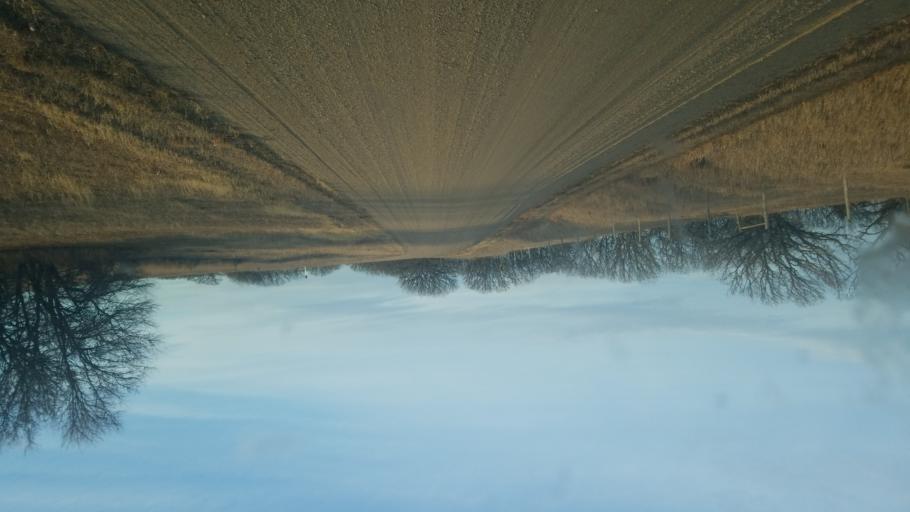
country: US
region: Nebraska
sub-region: Knox County
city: Center
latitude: 42.6920
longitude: -97.7805
